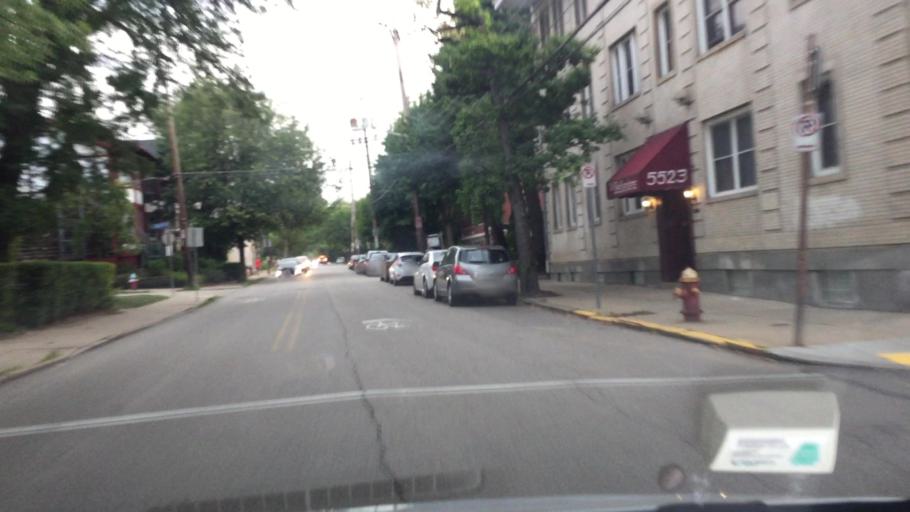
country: US
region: Pennsylvania
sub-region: Allegheny County
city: Bloomfield
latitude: 40.4537
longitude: -79.9348
